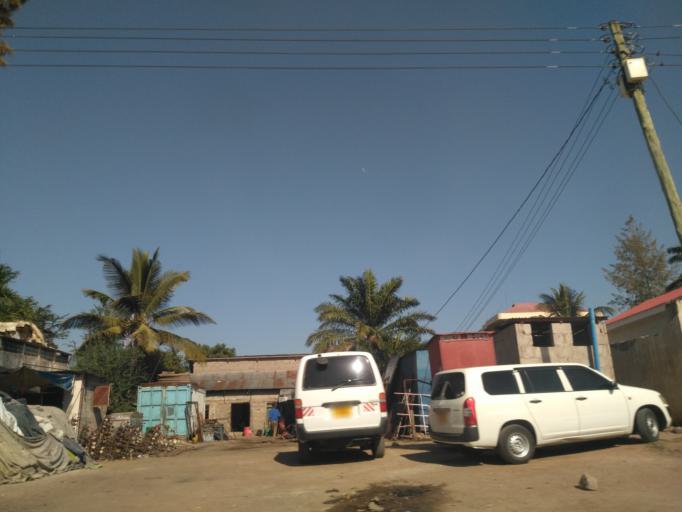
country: TZ
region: Mwanza
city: Mwanza
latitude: -2.5054
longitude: 32.8997
